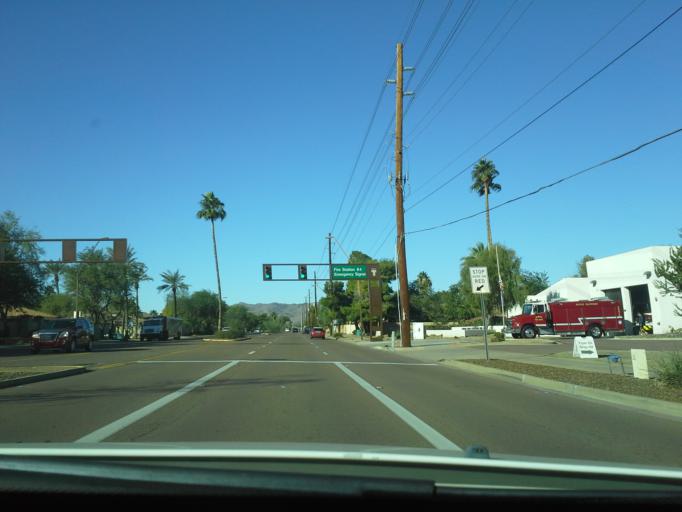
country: US
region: Arizona
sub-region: Maricopa County
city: Guadalupe
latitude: 33.3493
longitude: -111.9324
